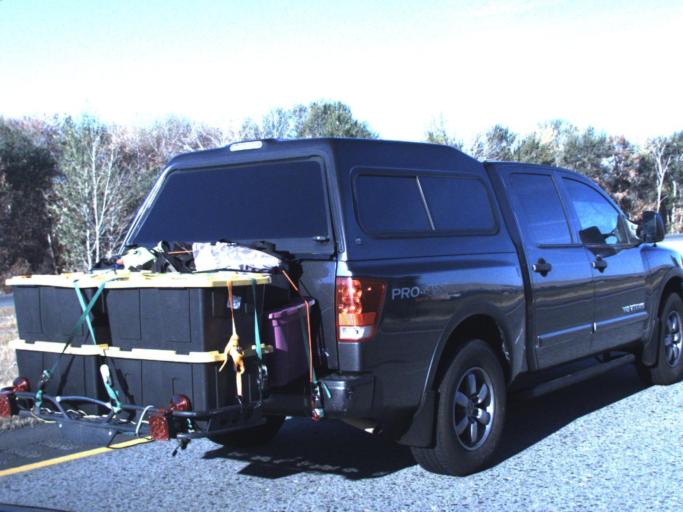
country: US
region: Washington
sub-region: Yakima County
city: Wapato
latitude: 46.4502
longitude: -120.3584
